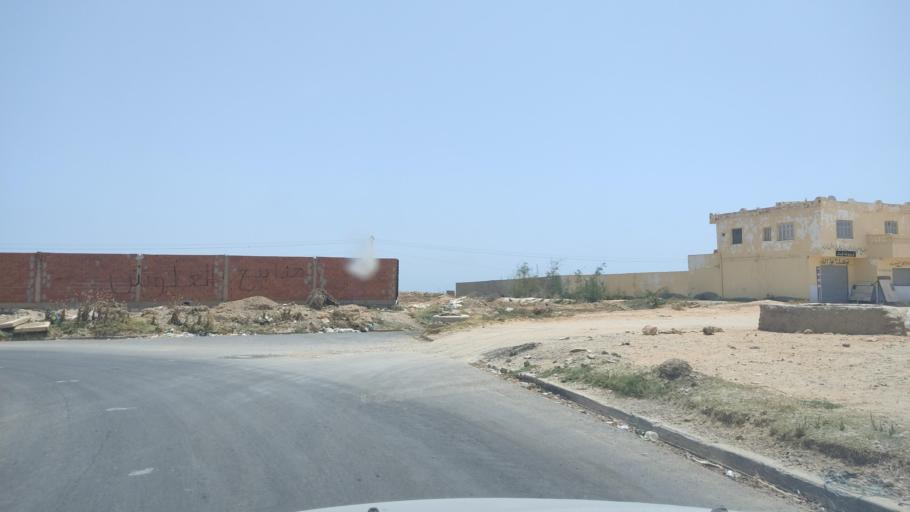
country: TN
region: Safaqis
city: Sfax
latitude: 34.6615
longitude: 10.7029
